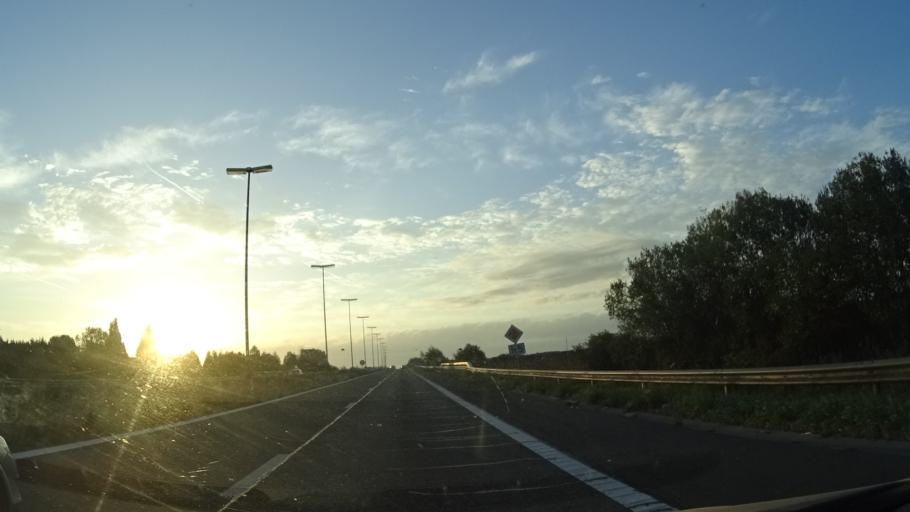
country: BE
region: Wallonia
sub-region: Province du Hainaut
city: Chasse Royale
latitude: 50.4108
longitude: 3.9371
